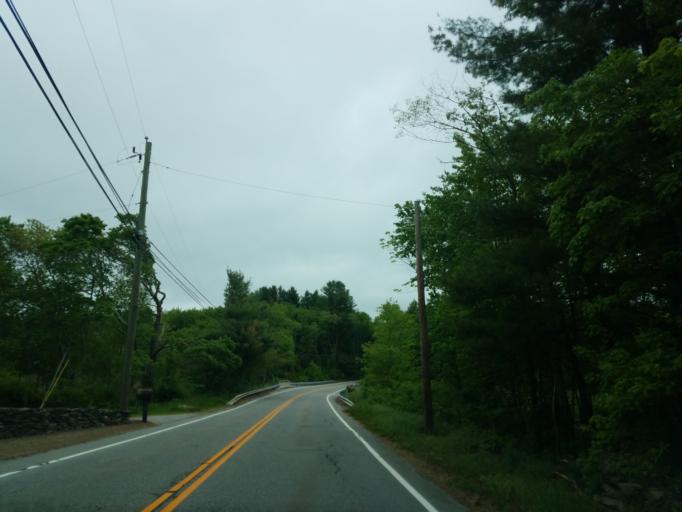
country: US
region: Connecticut
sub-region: Windham County
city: Quinebaug
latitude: 41.9957
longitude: -71.9908
